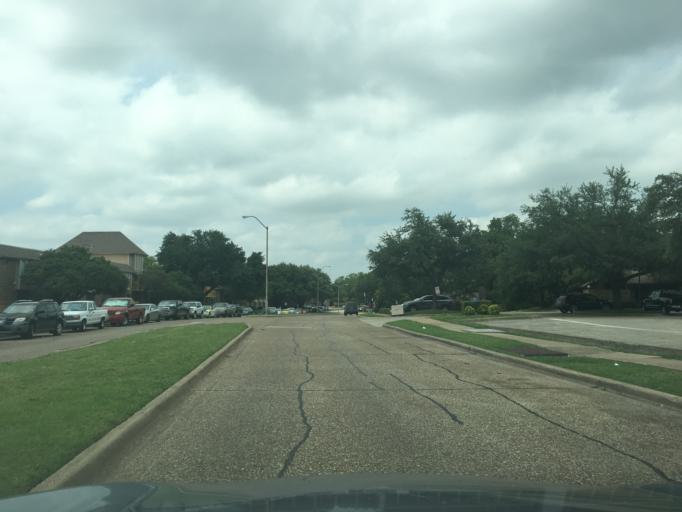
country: US
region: Texas
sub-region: Dallas County
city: Richardson
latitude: 32.9414
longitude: -96.7640
